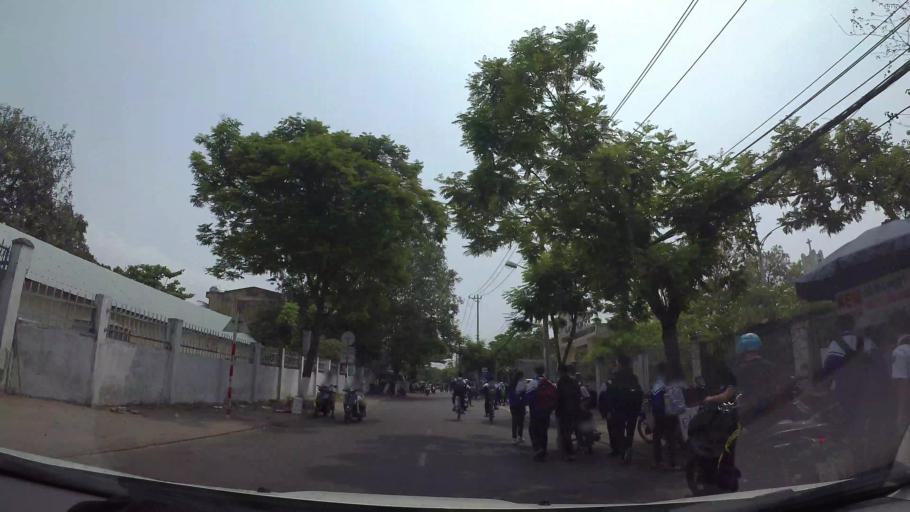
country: VN
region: Da Nang
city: Da Nang
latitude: 16.1016
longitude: 108.2485
